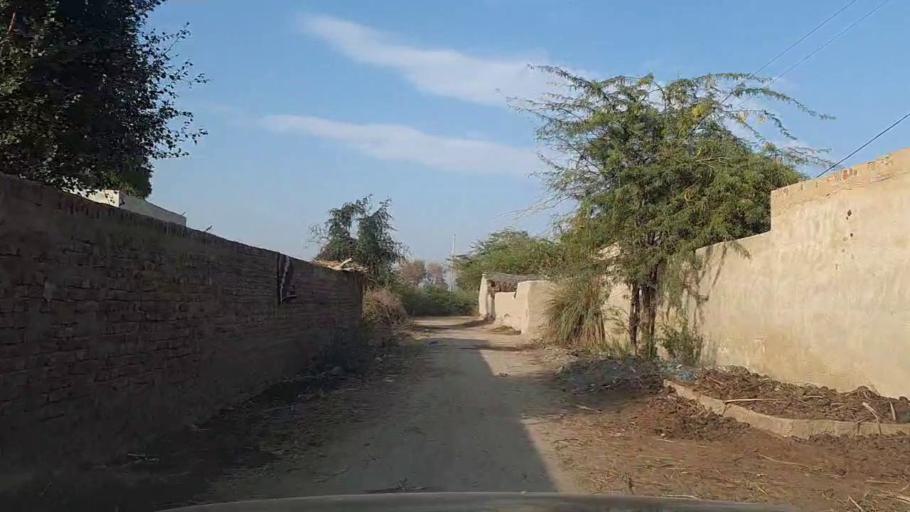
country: PK
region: Sindh
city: Daur
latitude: 26.4125
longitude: 68.4363
